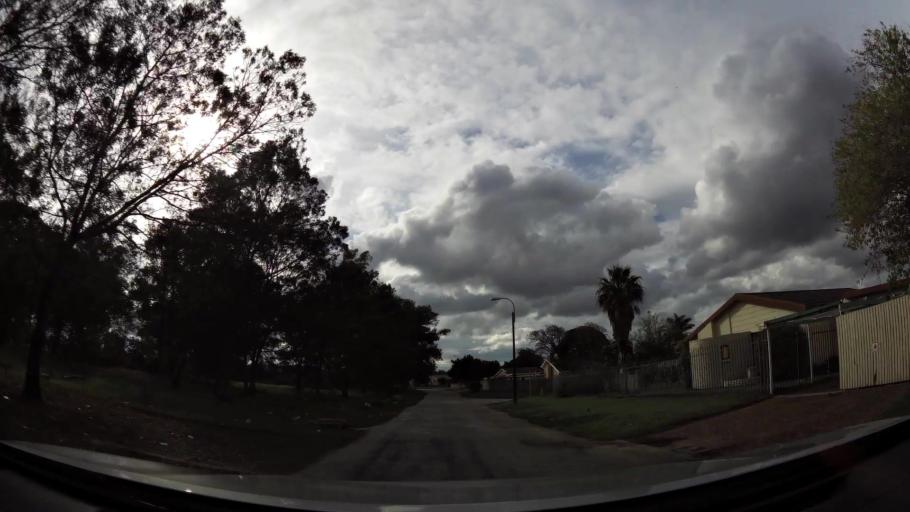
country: ZA
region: Eastern Cape
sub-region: Nelson Mandela Bay Metropolitan Municipality
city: Port Elizabeth
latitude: -33.9379
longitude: 25.4960
